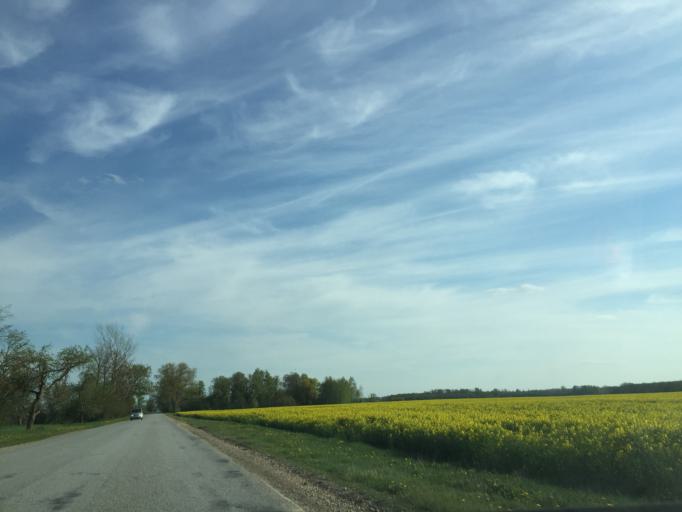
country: LV
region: Bauskas Rajons
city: Bauska
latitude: 56.3599
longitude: 24.2313
